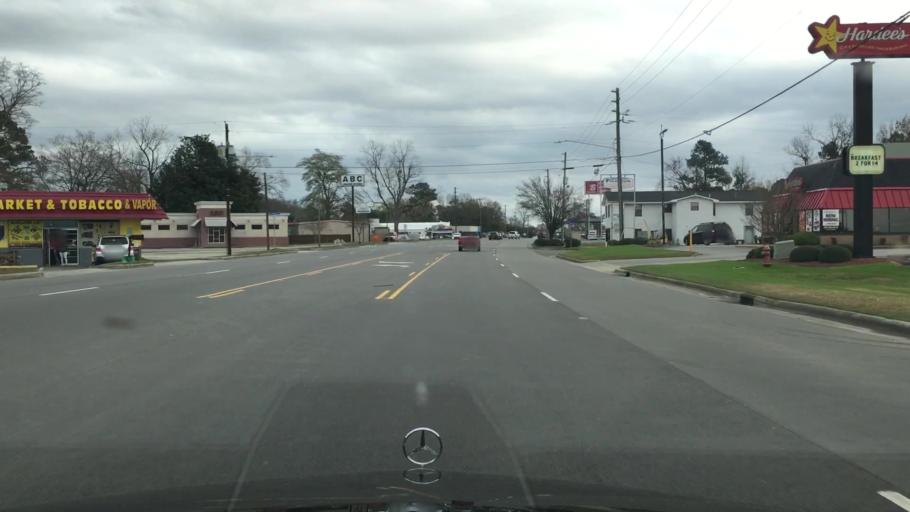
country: US
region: North Carolina
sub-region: Onslow County
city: Richlands
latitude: 34.9035
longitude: -77.5552
